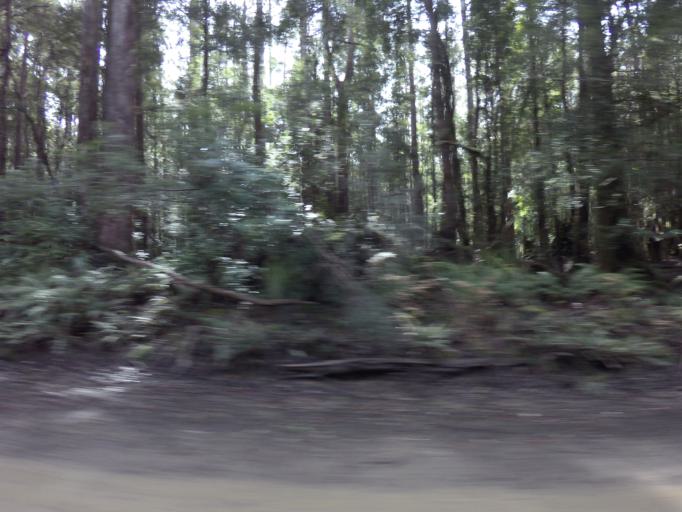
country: AU
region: Tasmania
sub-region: Huon Valley
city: Geeveston
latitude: -43.3845
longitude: 146.8440
